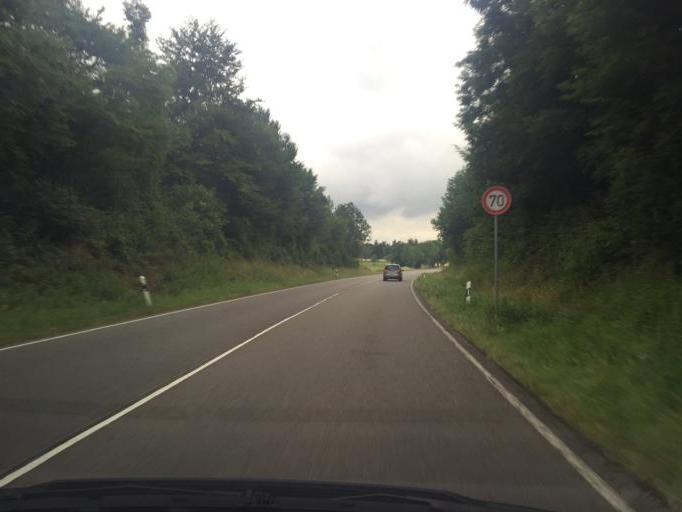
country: DE
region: Baden-Wuerttemberg
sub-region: Karlsruhe Region
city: Bretten
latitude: 48.9989
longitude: 8.7184
